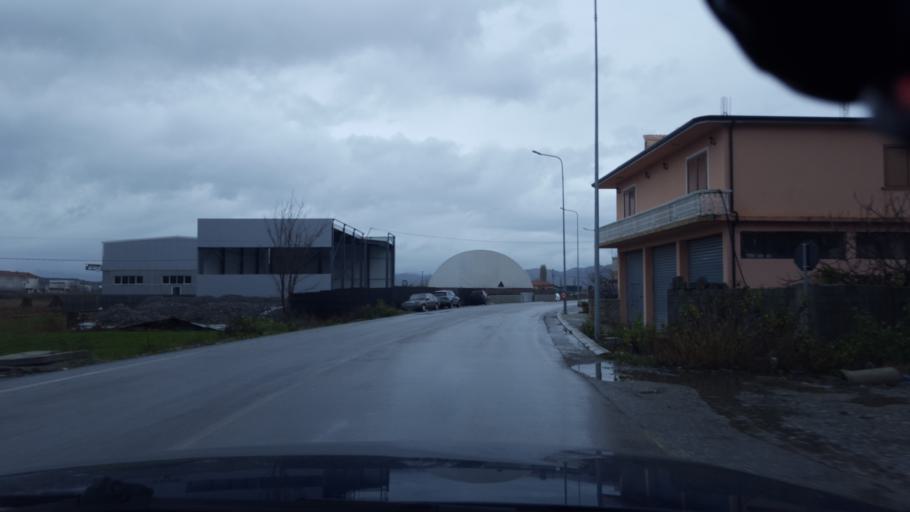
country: AL
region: Shkoder
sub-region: Rrethi i Shkodres
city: Berdica e Madhe
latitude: 42.0309
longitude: 19.4978
